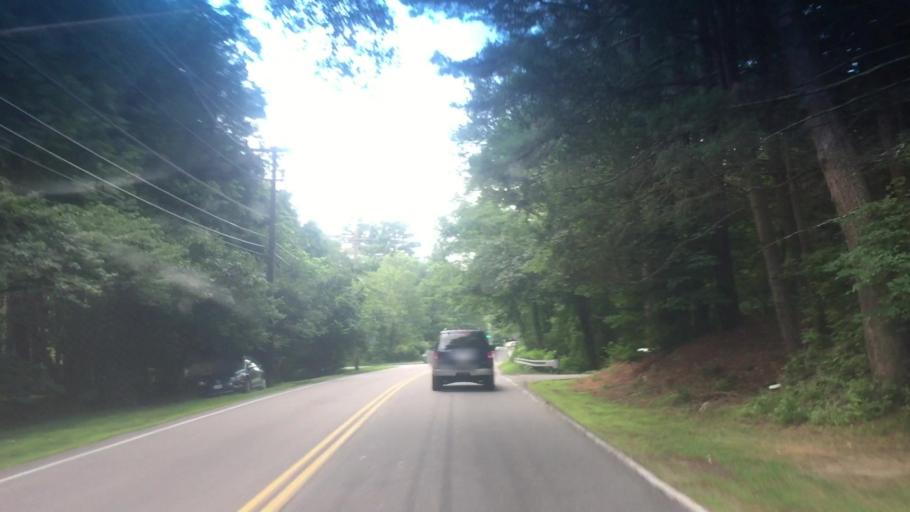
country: US
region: Massachusetts
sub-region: Norfolk County
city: Medfield
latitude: 42.1738
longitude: -71.2988
